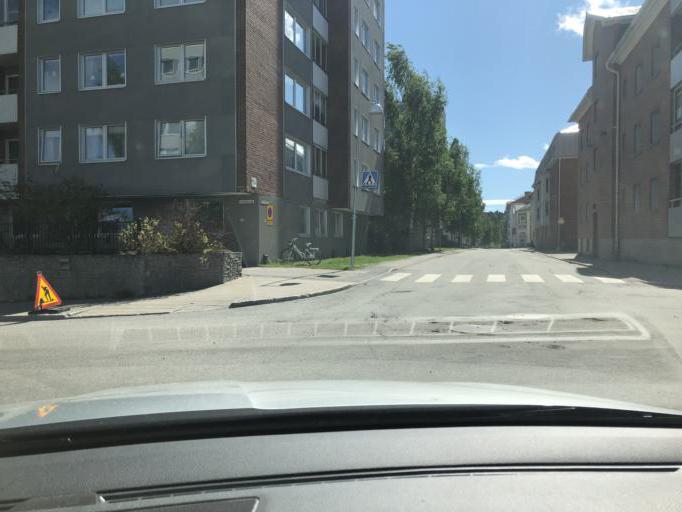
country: SE
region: Norrbotten
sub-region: Pitea Kommun
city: Pitea
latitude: 65.3165
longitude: 21.4843
